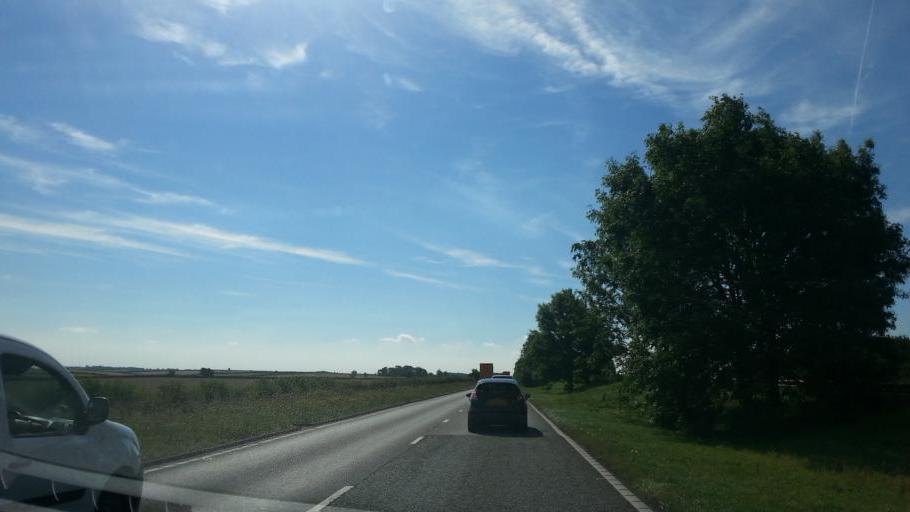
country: GB
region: England
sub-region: District of Rutland
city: Tickencote
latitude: 52.6861
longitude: -0.5526
